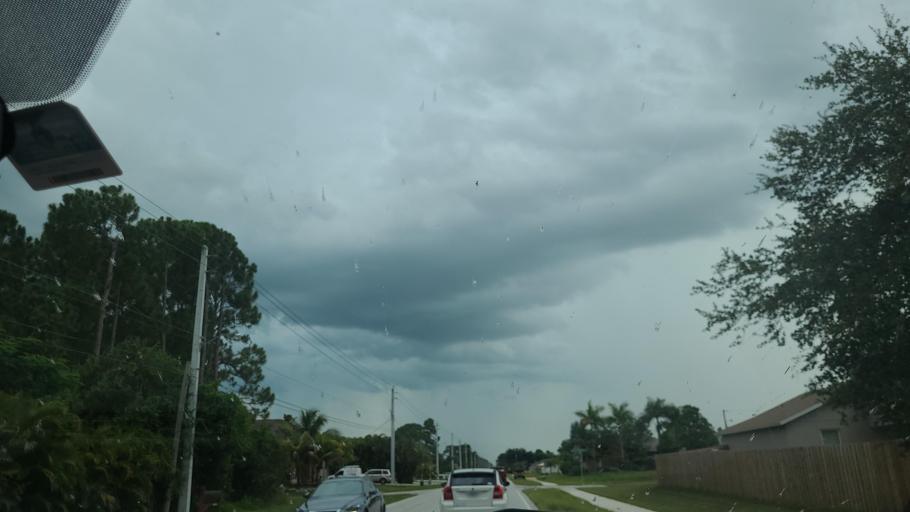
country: US
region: Florida
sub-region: Saint Lucie County
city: Port Saint Lucie
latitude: 27.2394
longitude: -80.3997
